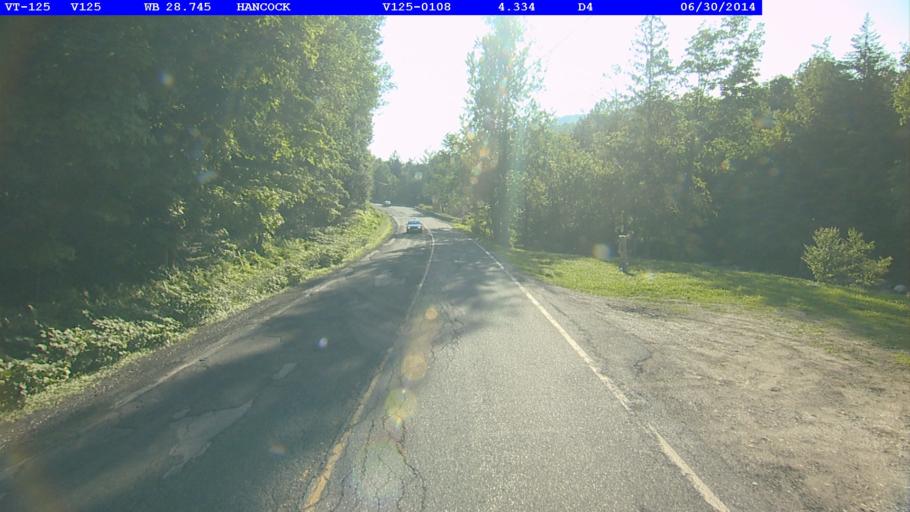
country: US
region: Vermont
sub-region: Orange County
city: Randolph
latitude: 43.9293
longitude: -72.8967
